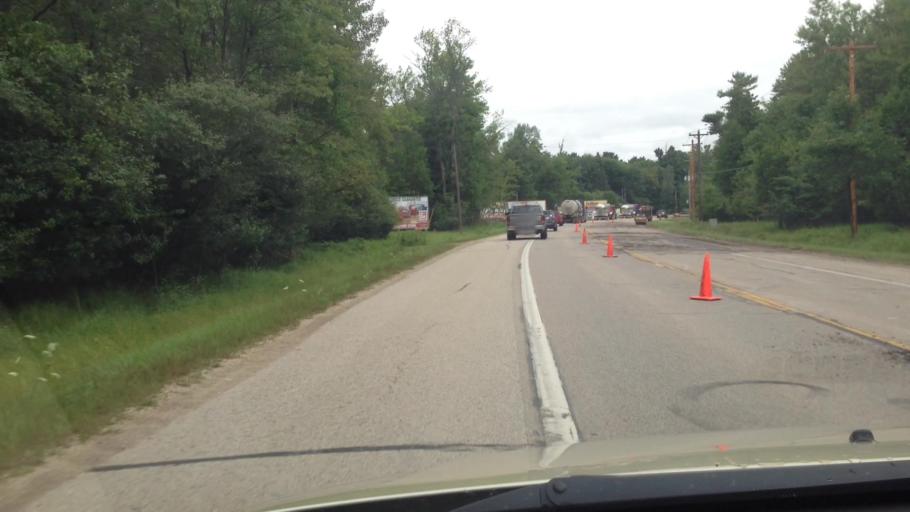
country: US
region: Michigan
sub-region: Delta County
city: Escanaba
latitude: 45.7037
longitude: -87.1010
